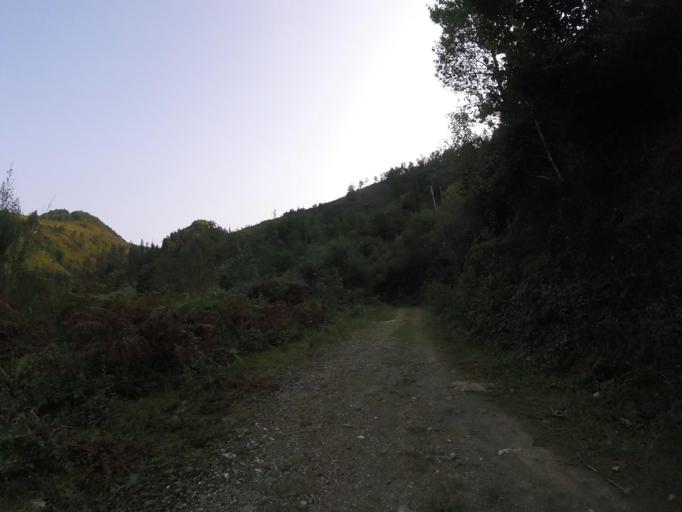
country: ES
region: Navarre
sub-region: Provincia de Navarra
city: Arano
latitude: 43.2533
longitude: -1.8438
